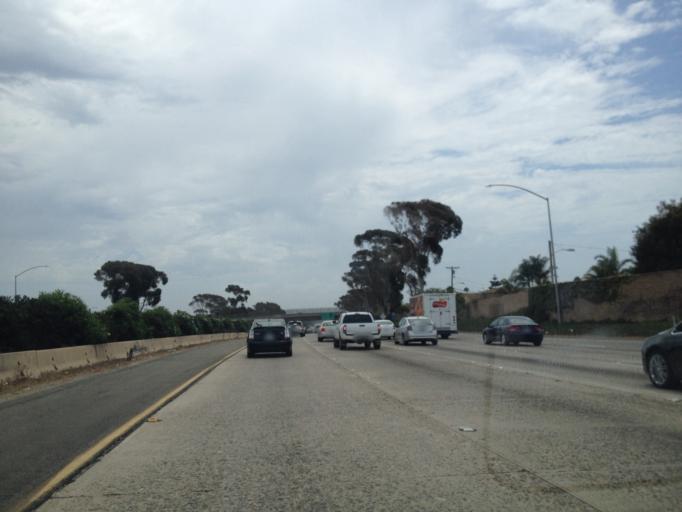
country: US
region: California
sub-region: San Diego County
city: Oceanside
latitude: 33.1983
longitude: -117.3692
